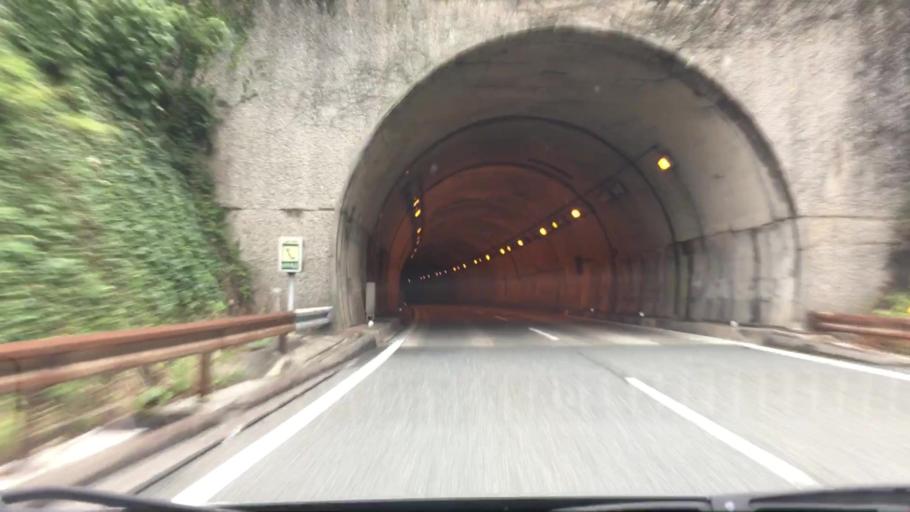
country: JP
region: Okayama
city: Niimi
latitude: 34.9935
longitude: 133.4572
